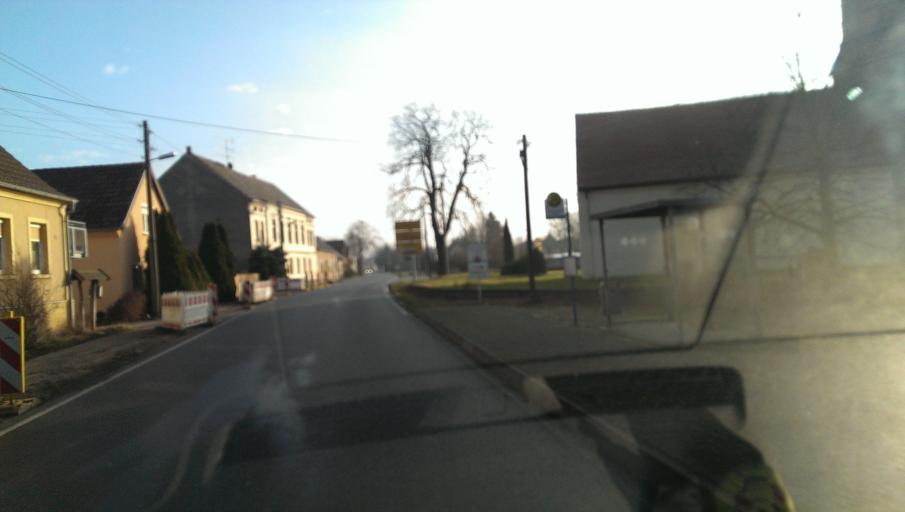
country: DE
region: Brandenburg
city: Schilda
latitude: 51.6052
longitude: 13.3408
